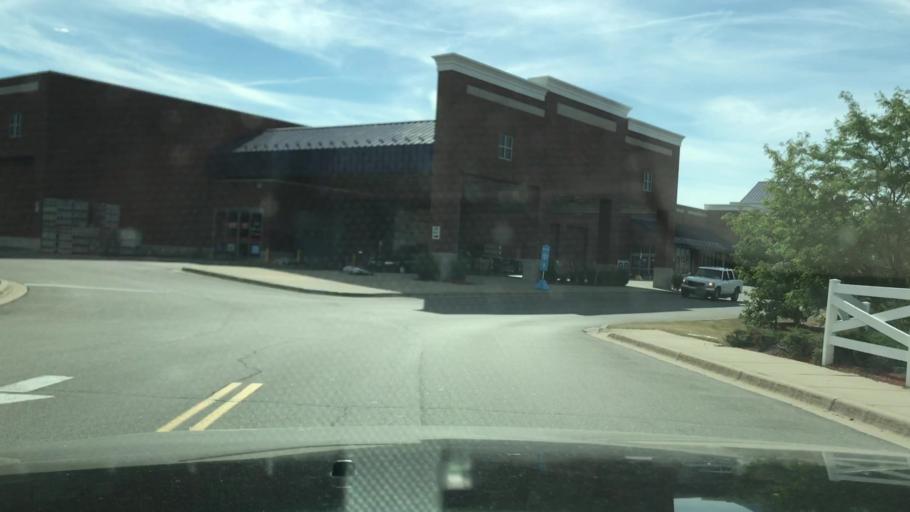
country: US
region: Michigan
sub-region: Kent County
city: East Grand Rapids
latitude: 42.9106
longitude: -85.5837
